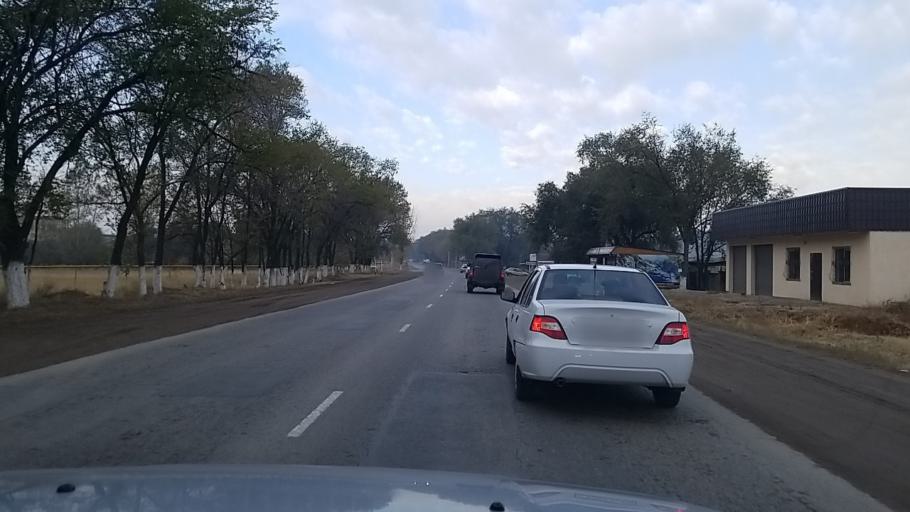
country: KZ
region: Almaty Oblysy
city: Burunday
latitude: 43.3589
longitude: 76.7674
